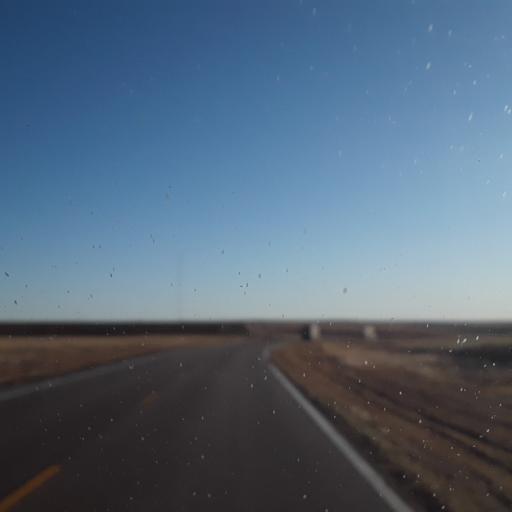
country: US
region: Kansas
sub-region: Wallace County
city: Sharon Springs
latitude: 39.1161
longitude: -101.7282
